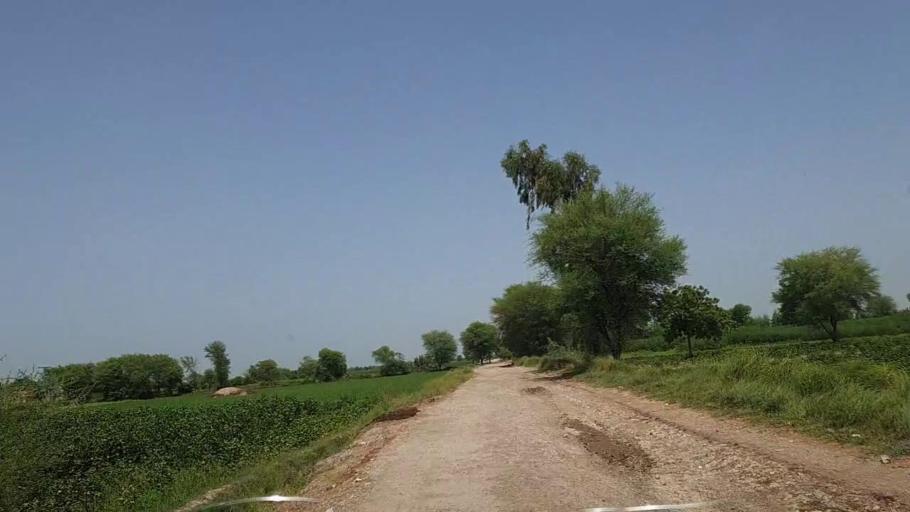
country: PK
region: Sindh
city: Kandiaro
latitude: 27.0142
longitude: 68.1573
